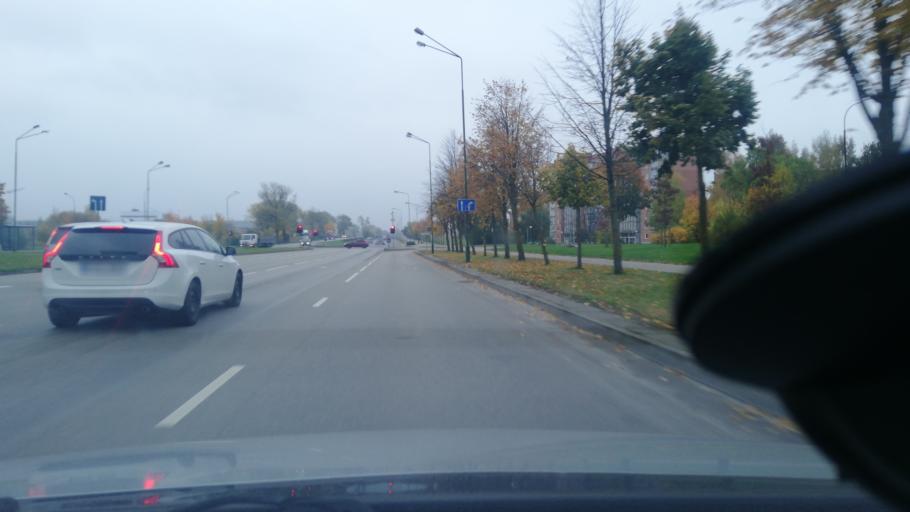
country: LT
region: Klaipedos apskritis
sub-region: Klaipeda
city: Klaipeda
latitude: 55.6728
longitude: 21.1984
